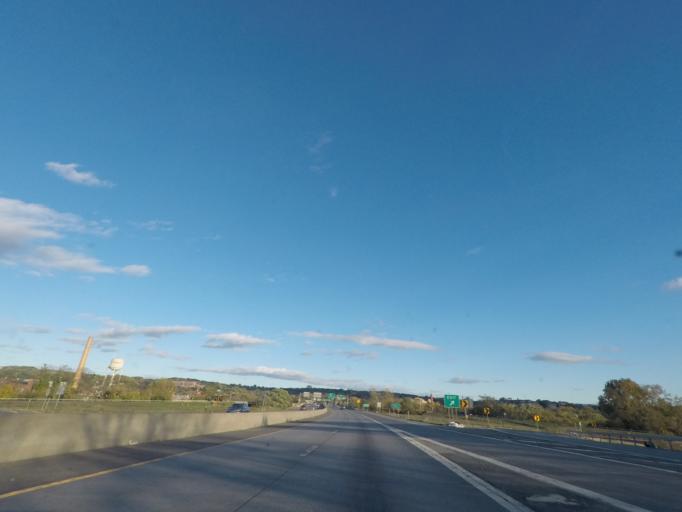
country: US
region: New York
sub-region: Albany County
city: Green Island
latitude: 42.7421
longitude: -73.6968
